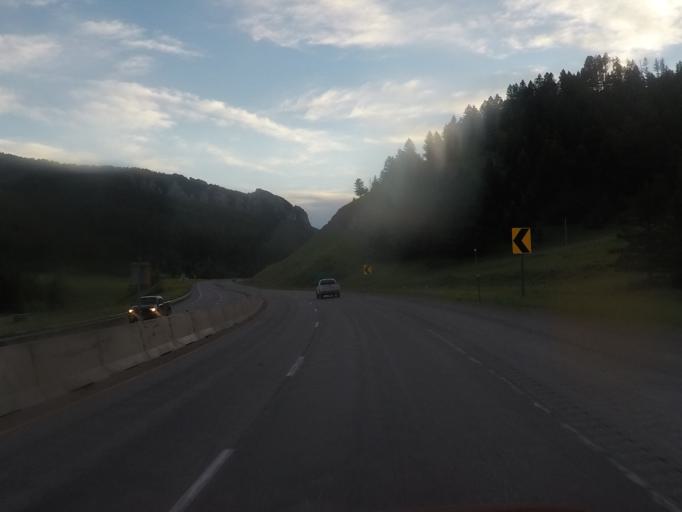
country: US
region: Montana
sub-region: Gallatin County
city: Bozeman
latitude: 45.6486
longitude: -110.8715
